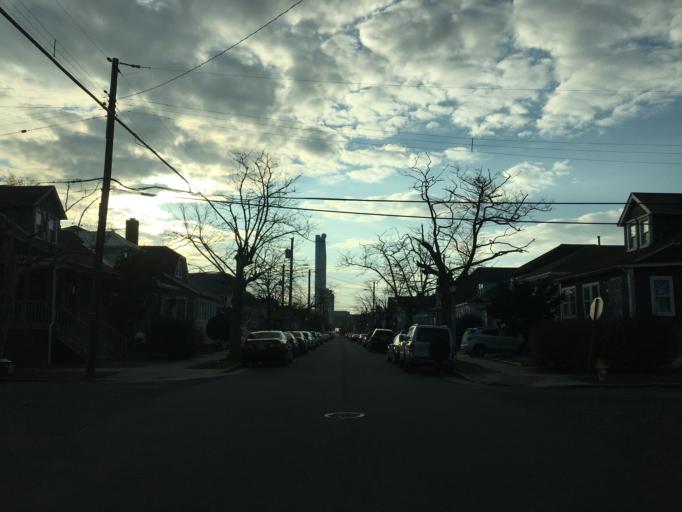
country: US
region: New Jersey
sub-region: Atlantic County
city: Atlantic City
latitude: 39.3731
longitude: -74.4227
